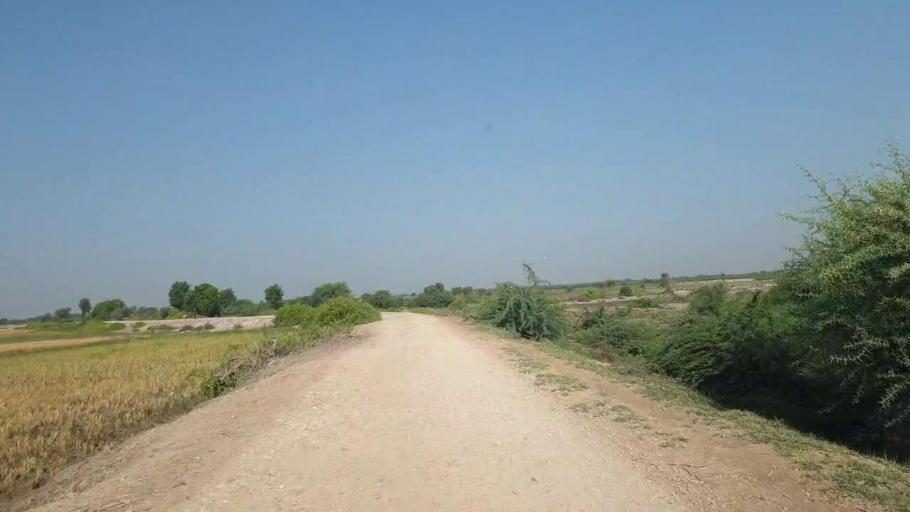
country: PK
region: Sindh
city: Badin
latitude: 24.5199
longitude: 68.7746
